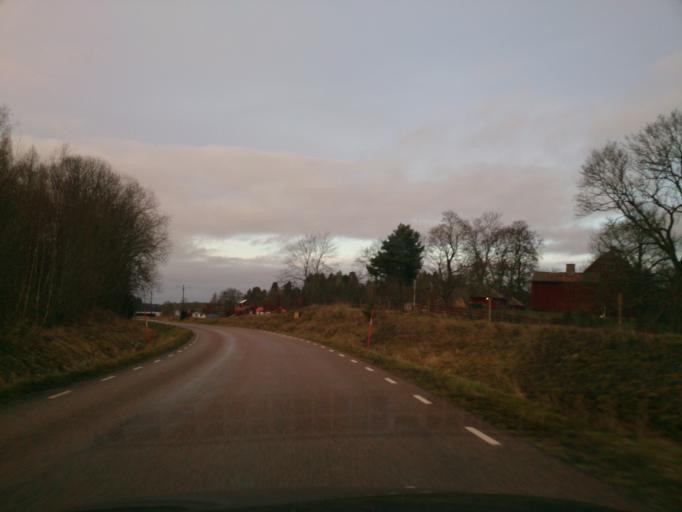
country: SE
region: OEstergoetland
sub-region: Atvidabergs Kommun
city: Atvidaberg
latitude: 58.3336
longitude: 16.0284
